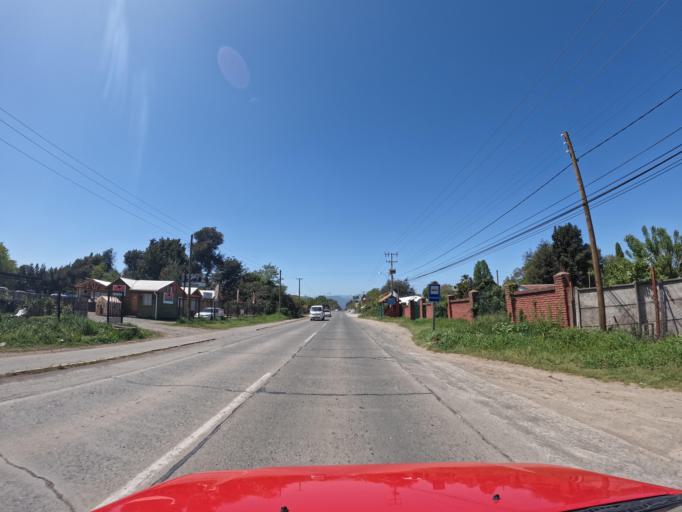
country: CL
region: Maule
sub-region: Provincia de Linares
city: Linares
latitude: -35.8323
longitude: -71.5289
